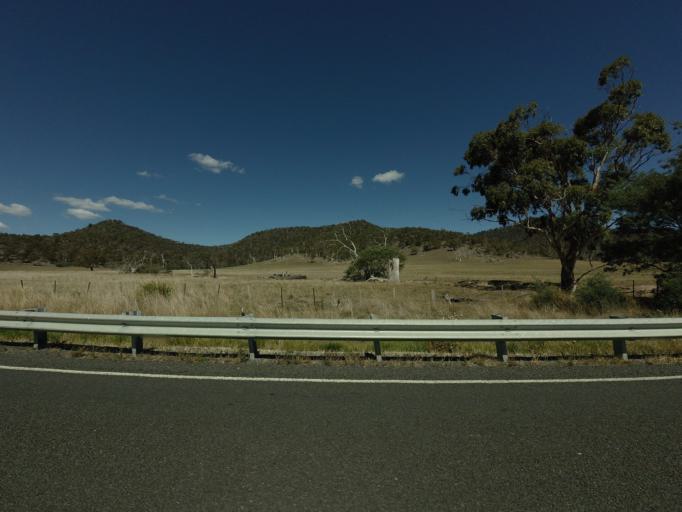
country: AU
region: Tasmania
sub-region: Break O'Day
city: St Helens
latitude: -41.6907
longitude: 147.8757
